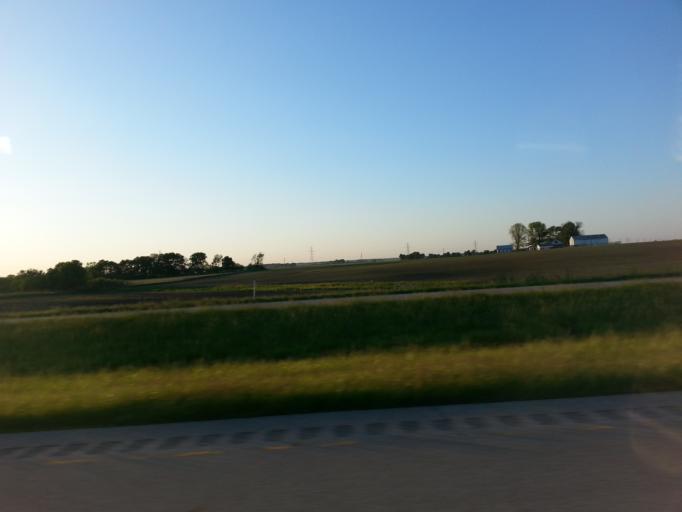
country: US
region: Indiana
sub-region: Fountain County
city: Veedersburg
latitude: 40.1222
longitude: -87.3274
